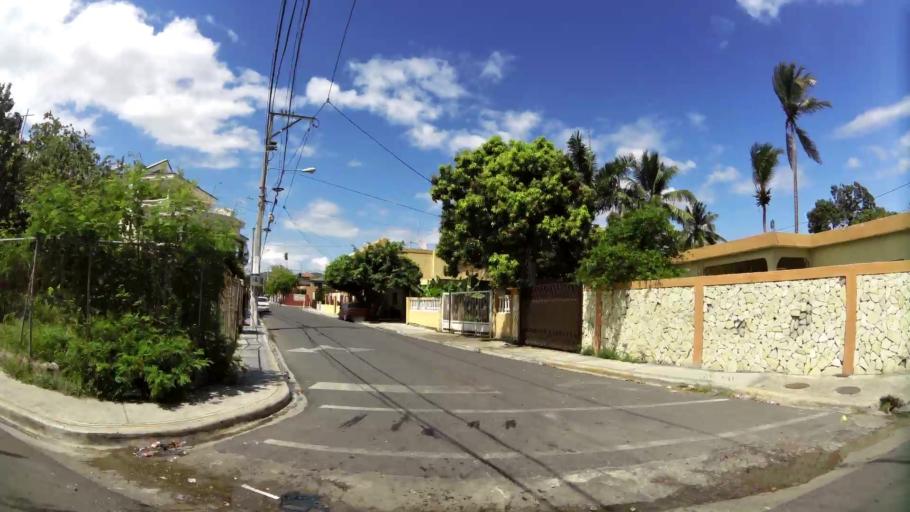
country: DO
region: San Cristobal
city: San Cristobal
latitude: 18.4200
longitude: -70.0956
